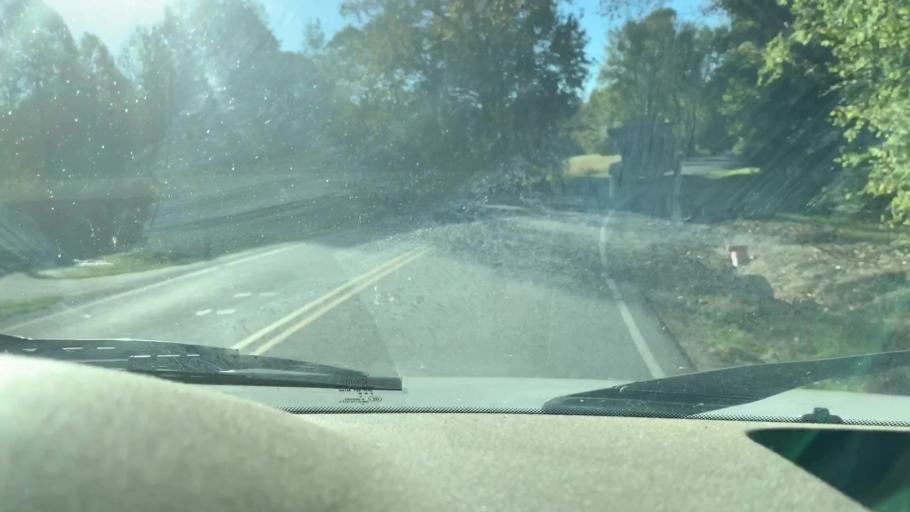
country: US
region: North Carolina
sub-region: Mecklenburg County
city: Huntersville
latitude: 35.4339
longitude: -80.7629
